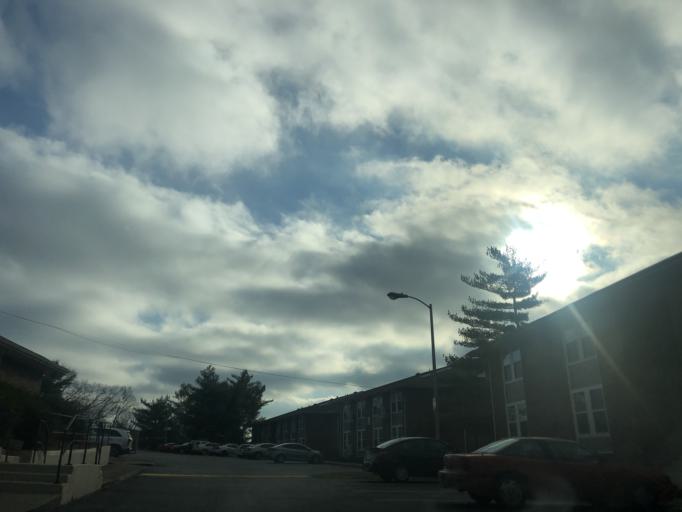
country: US
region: Tennessee
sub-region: Davidson County
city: Nashville
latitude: 36.2151
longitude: -86.7943
